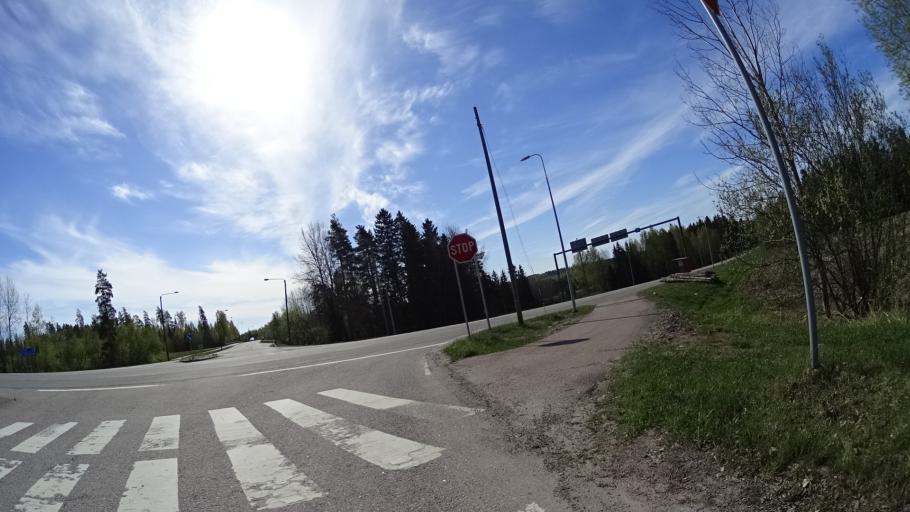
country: FI
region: Uusimaa
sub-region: Helsinki
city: Nurmijaervi
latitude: 60.4377
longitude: 24.8304
